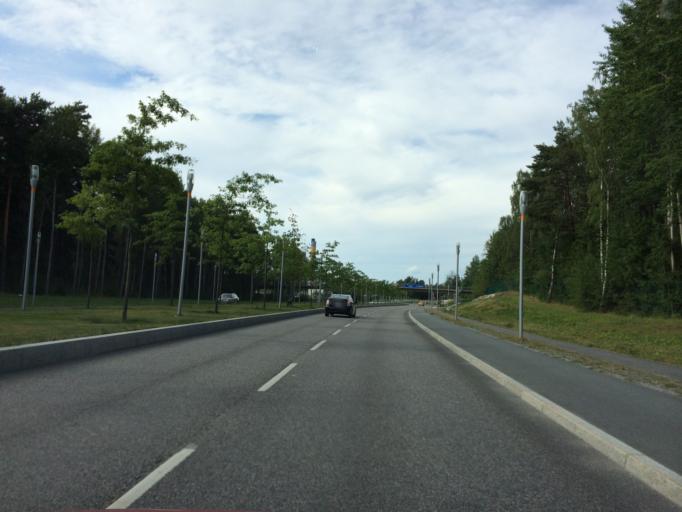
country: SE
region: Stockholm
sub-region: Stockholms Kommun
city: Kista
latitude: 59.4105
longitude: 17.9341
